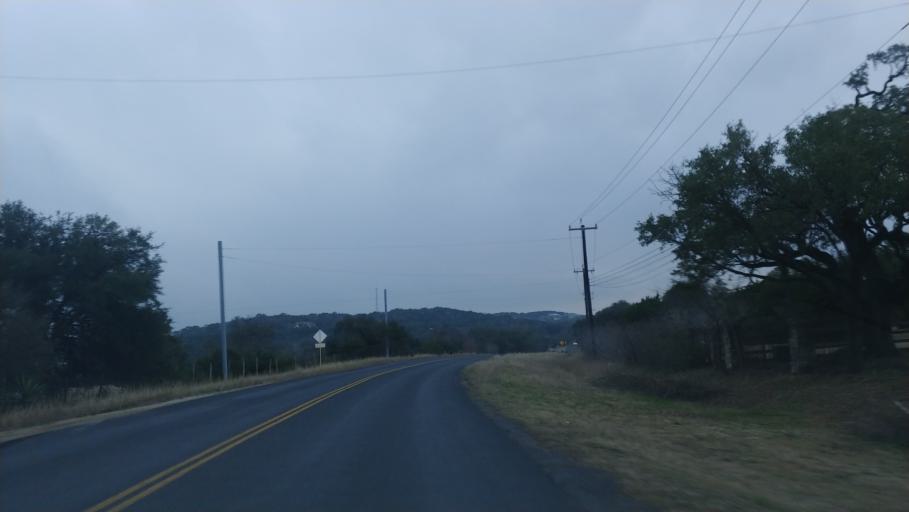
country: US
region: Texas
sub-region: Bexar County
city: Scenic Oaks
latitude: 29.6768
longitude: -98.6745
